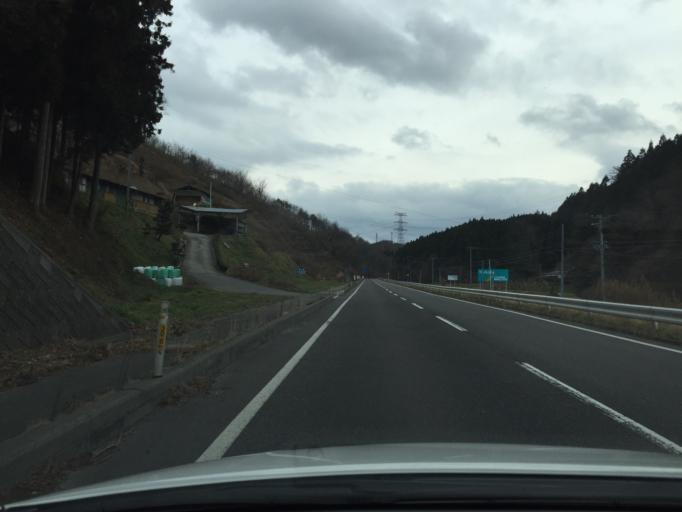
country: JP
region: Fukushima
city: Ishikawa
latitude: 37.1863
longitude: 140.6452
